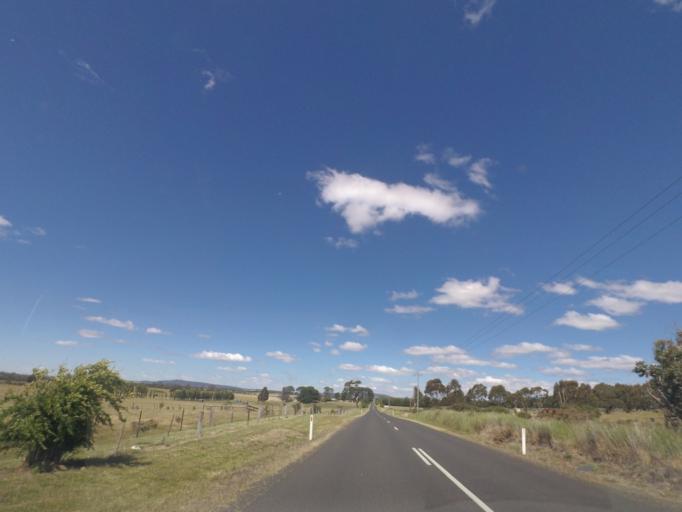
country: AU
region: Victoria
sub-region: Mount Alexander
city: Castlemaine
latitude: -37.2870
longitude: 144.4496
